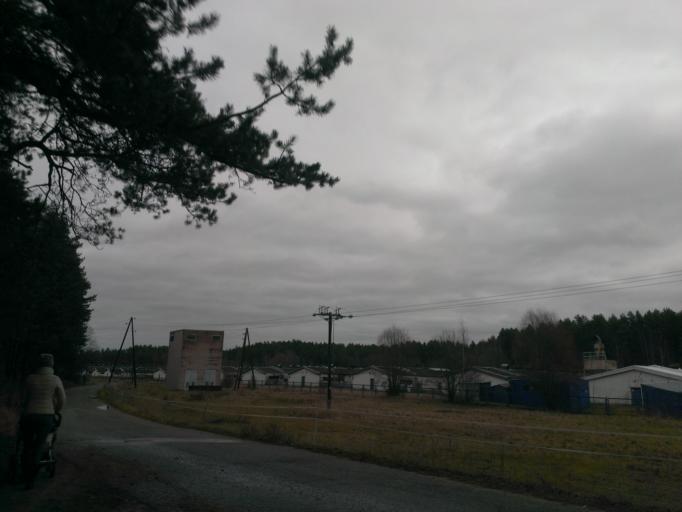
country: LV
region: Adazi
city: Adazi
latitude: 57.0574
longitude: 24.3528
